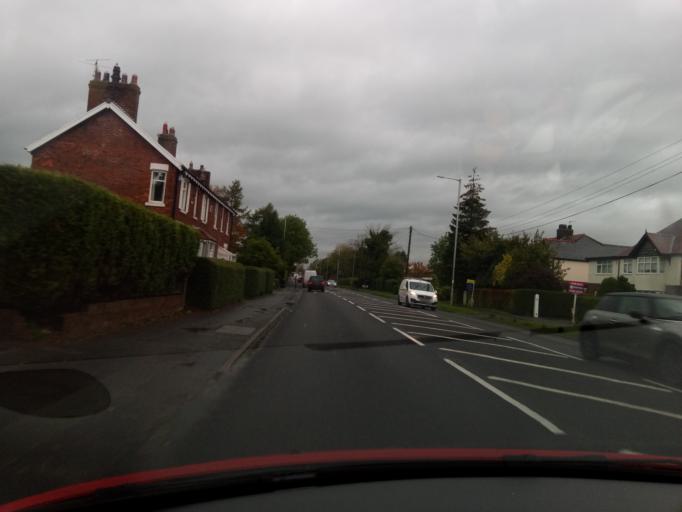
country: GB
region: England
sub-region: Lancashire
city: Catterall
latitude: 53.8331
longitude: -2.7383
